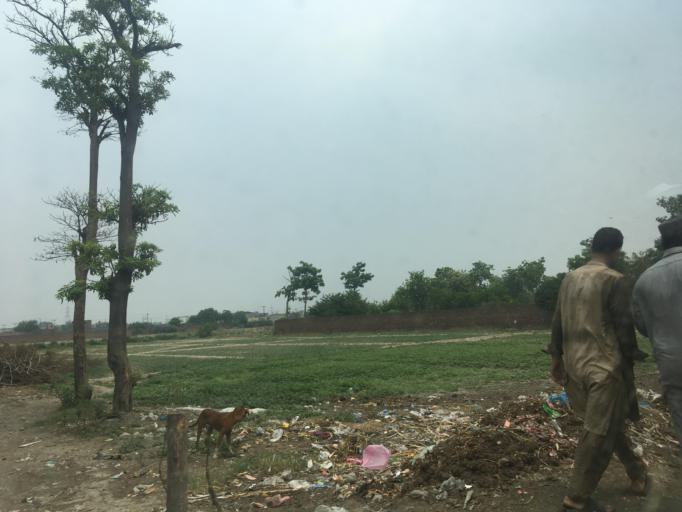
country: PK
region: Punjab
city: Lahore
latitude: 31.6157
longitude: 74.3675
